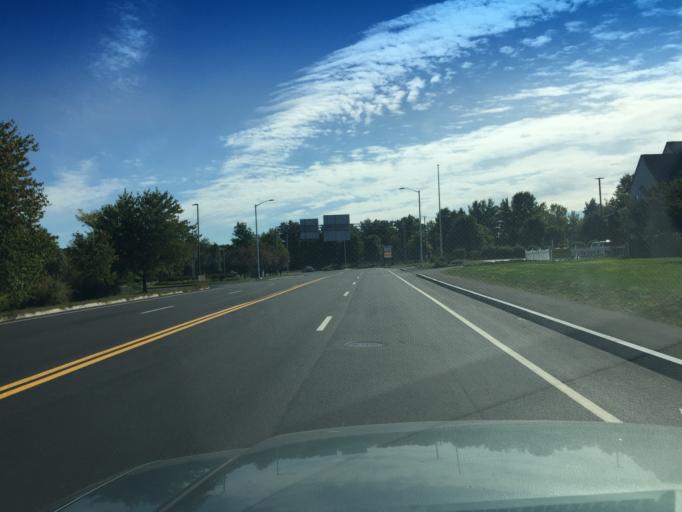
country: US
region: Massachusetts
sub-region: Worcester County
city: Berlin
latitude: 42.3501
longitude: -71.6226
